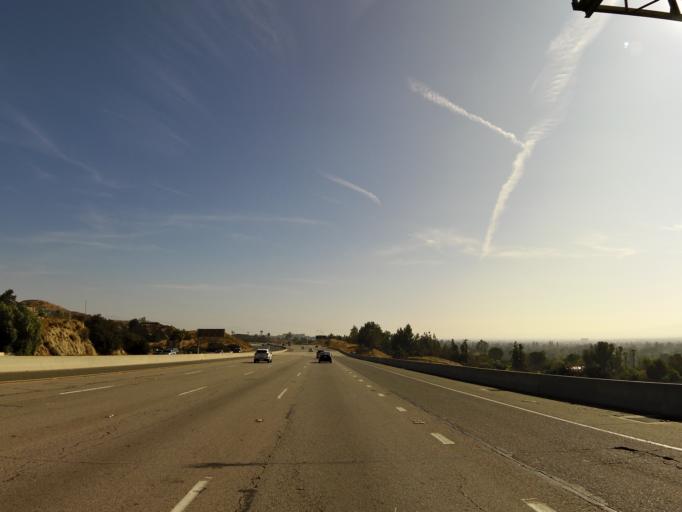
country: US
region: California
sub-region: Los Angeles County
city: Chatsworth
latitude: 34.2752
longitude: -118.5983
